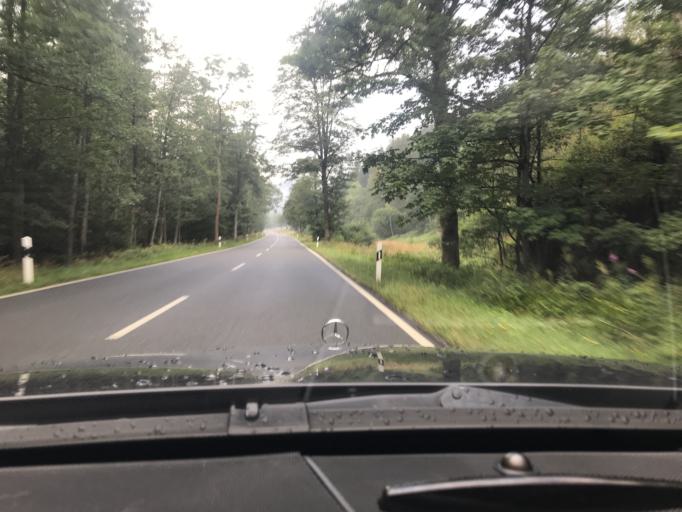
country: DE
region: Lower Saxony
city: Braunlage
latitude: 51.6897
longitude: 10.5714
